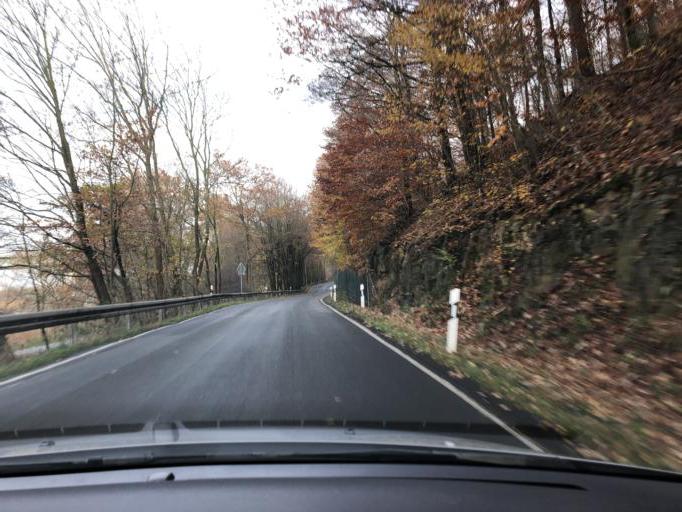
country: DE
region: Saxony
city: Nerchau
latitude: 51.2557
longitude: 12.7823
